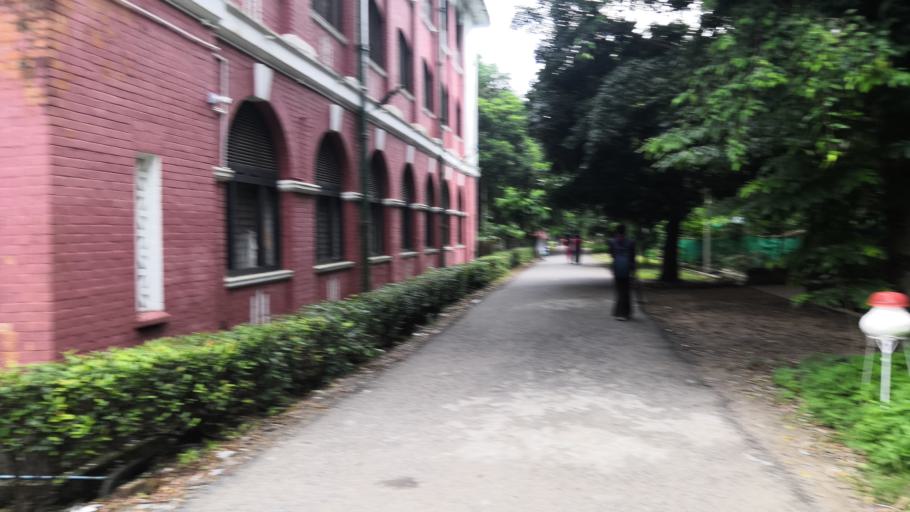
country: MM
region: Yangon
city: Yangon
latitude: 16.8302
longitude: 96.1337
